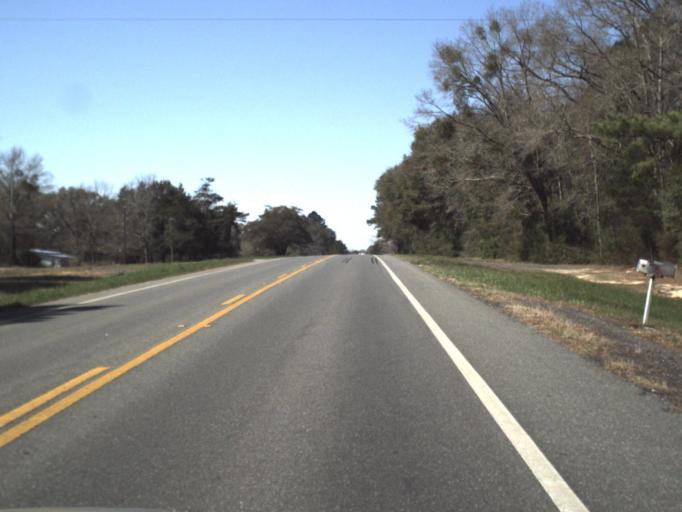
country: US
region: Florida
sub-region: Jackson County
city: Marianna
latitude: 30.7848
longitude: -85.3210
